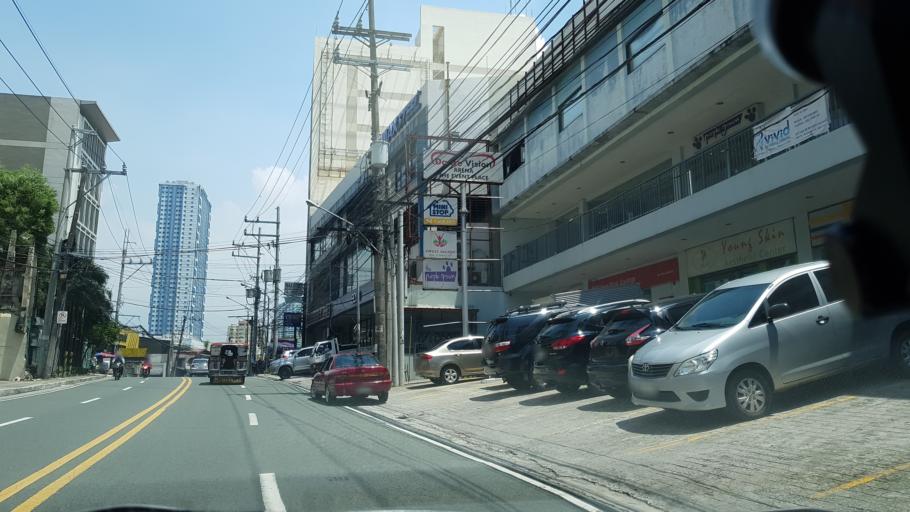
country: PH
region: Metro Manila
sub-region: San Juan
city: San Juan
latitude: 14.6100
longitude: 121.0303
